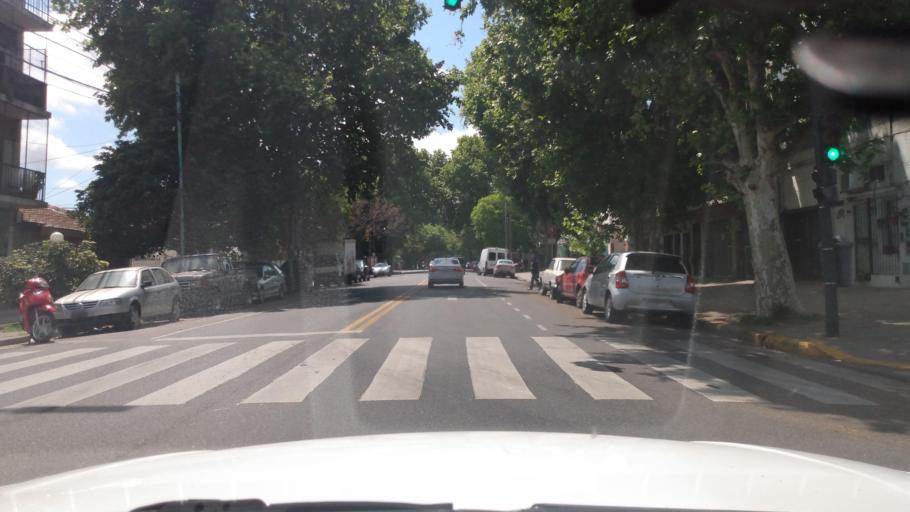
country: AR
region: Buenos Aires
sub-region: Partido de General San Martin
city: General San Martin
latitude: -34.5777
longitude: -58.5100
